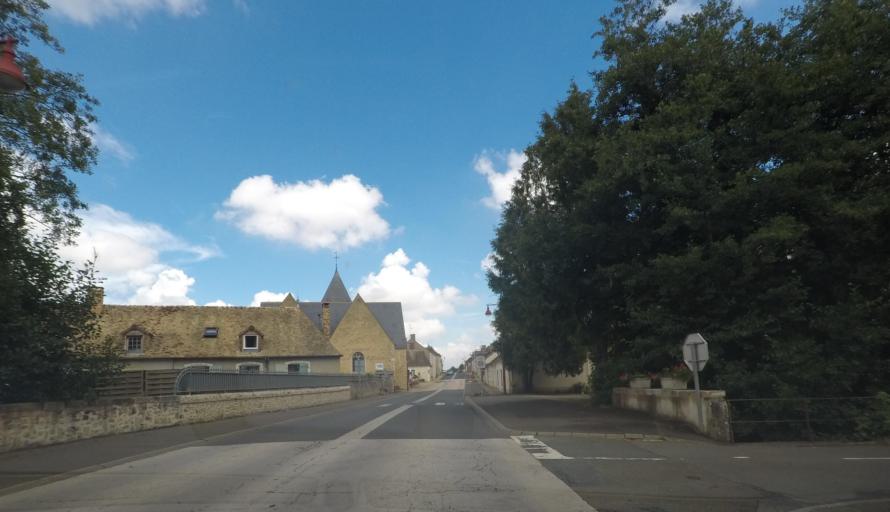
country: FR
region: Pays de la Loire
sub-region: Departement de la Sarthe
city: Bonnetable
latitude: 48.2259
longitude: 0.4293
